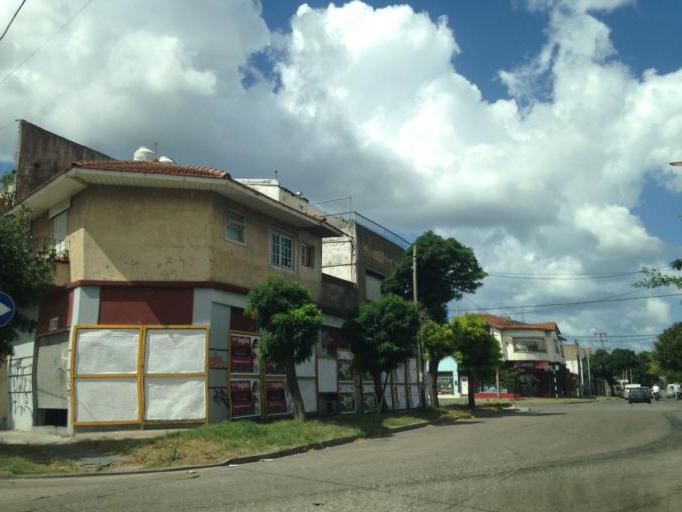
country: AR
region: Buenos Aires
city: Mar del Plata
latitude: -38.0194
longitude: -57.5726
